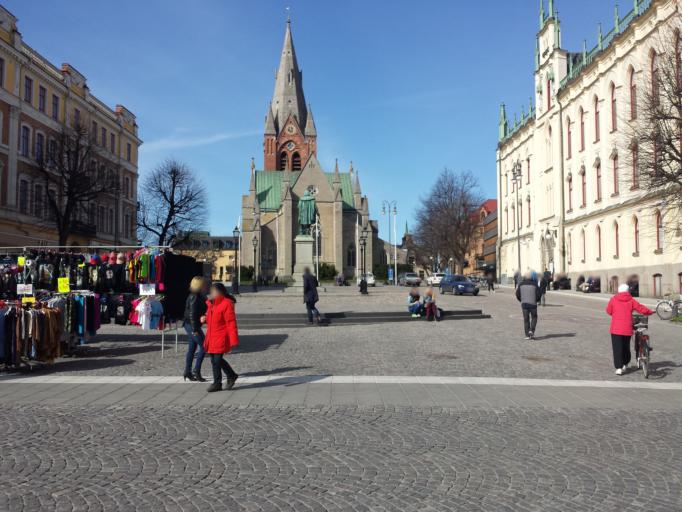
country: SE
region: OErebro
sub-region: Orebro Kommun
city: Orebro
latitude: 59.2719
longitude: 15.2132
